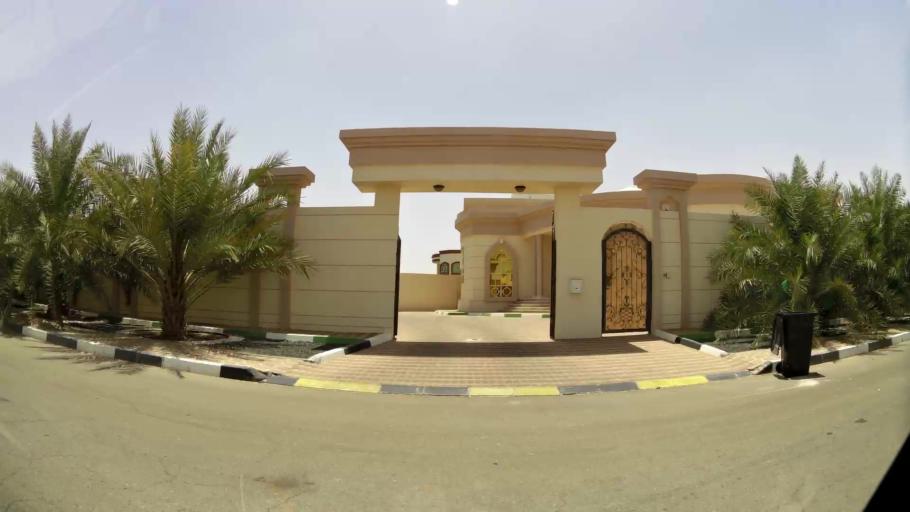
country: AE
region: Abu Dhabi
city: Al Ain
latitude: 24.2480
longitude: 55.7007
